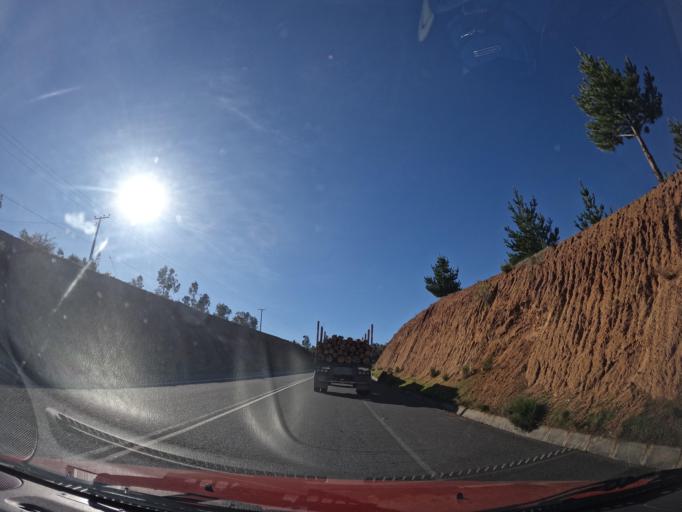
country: CL
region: Maule
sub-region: Provincia de Cauquenes
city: Cauquenes
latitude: -35.9342
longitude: -72.1947
